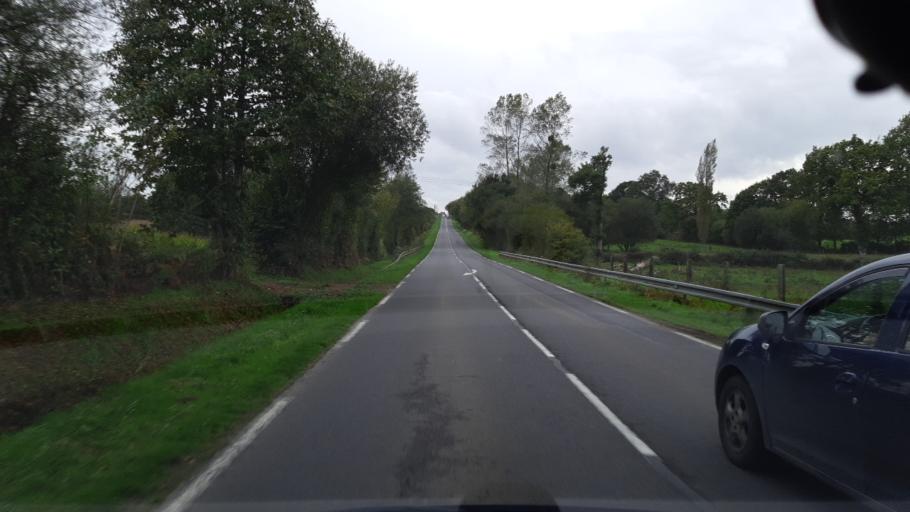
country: FR
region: Lower Normandy
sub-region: Departement de la Manche
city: Gavray
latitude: 48.9352
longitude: -1.3705
